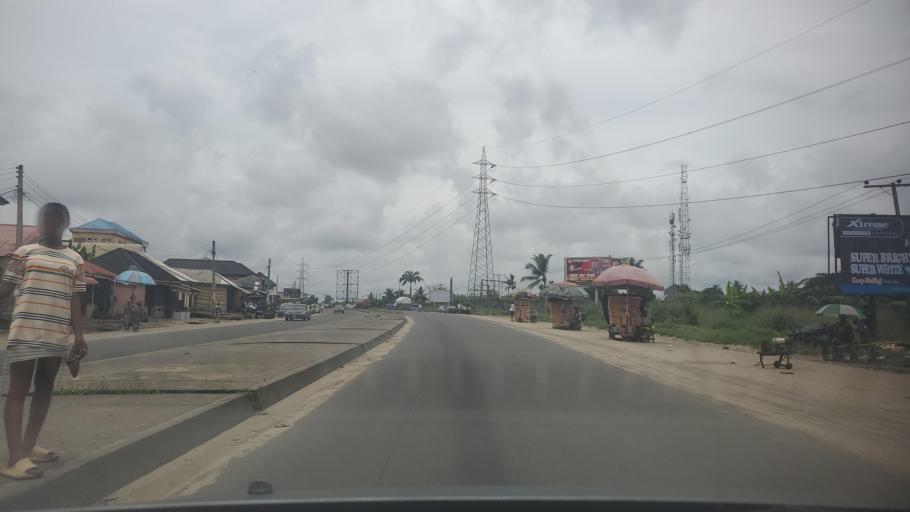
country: NG
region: Rivers
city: Emuoha
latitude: 4.8983
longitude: 6.9034
